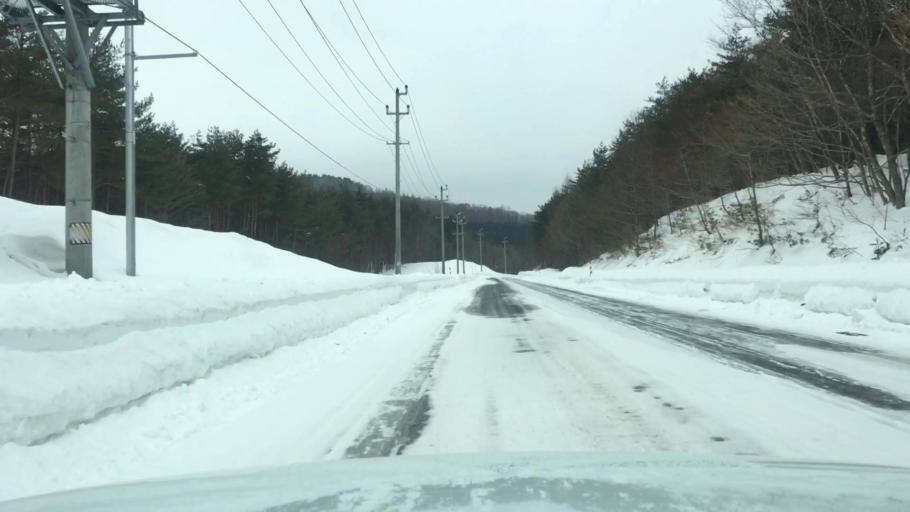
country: JP
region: Iwate
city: Shizukuishi
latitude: 39.9736
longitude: 141.0023
